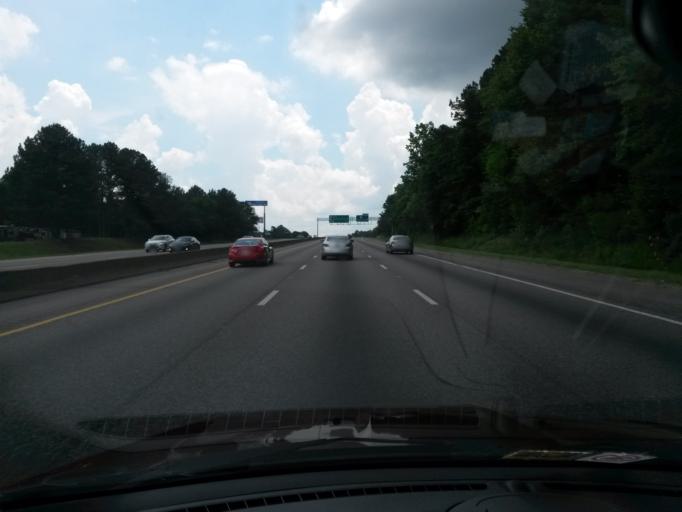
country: US
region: Virginia
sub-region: Chesterfield County
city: Bellwood
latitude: 37.4061
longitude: -77.4257
